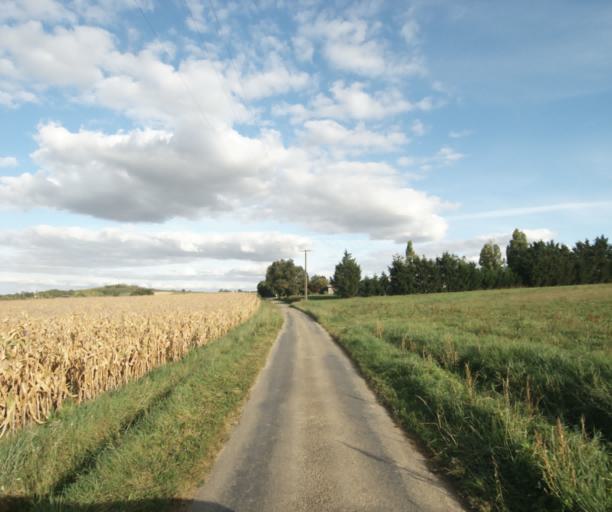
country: FR
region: Midi-Pyrenees
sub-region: Departement du Gers
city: Gondrin
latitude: 43.8906
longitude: 0.2871
